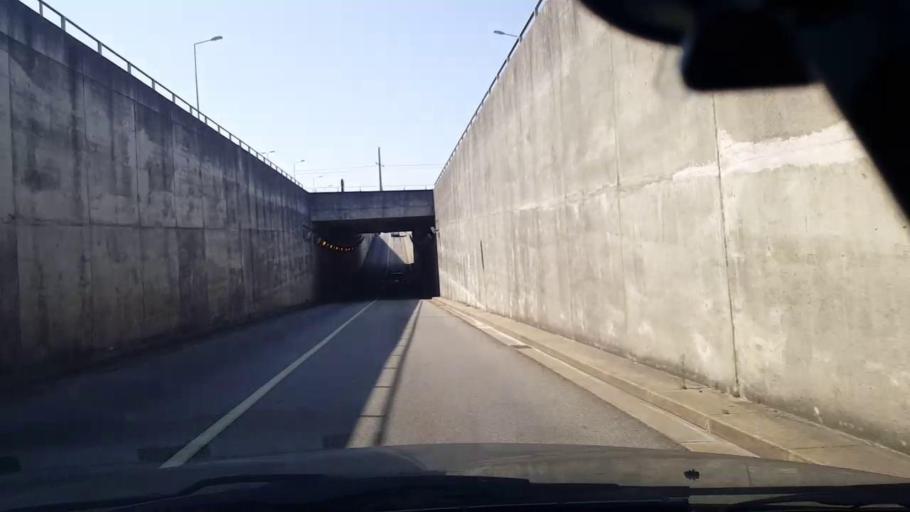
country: PT
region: Porto
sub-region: Vila do Conde
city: Vila do Conde
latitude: 41.3692
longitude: -8.7485
